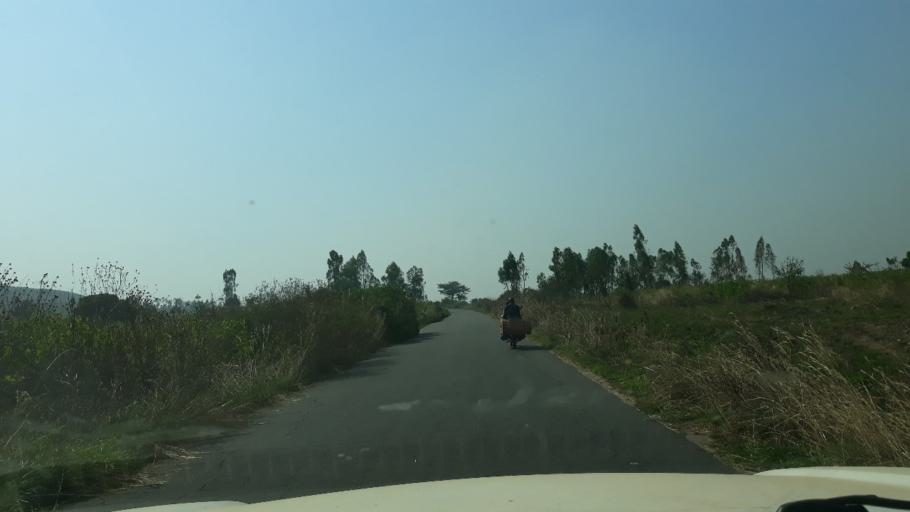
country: CD
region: South Kivu
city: Uvira
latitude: -3.2113
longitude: 29.1644
